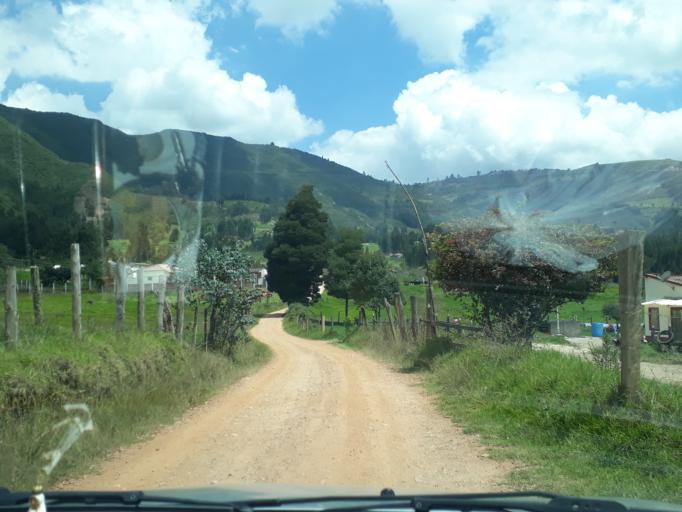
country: CO
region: Boyaca
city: Floresta
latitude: 5.8498
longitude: -72.9537
